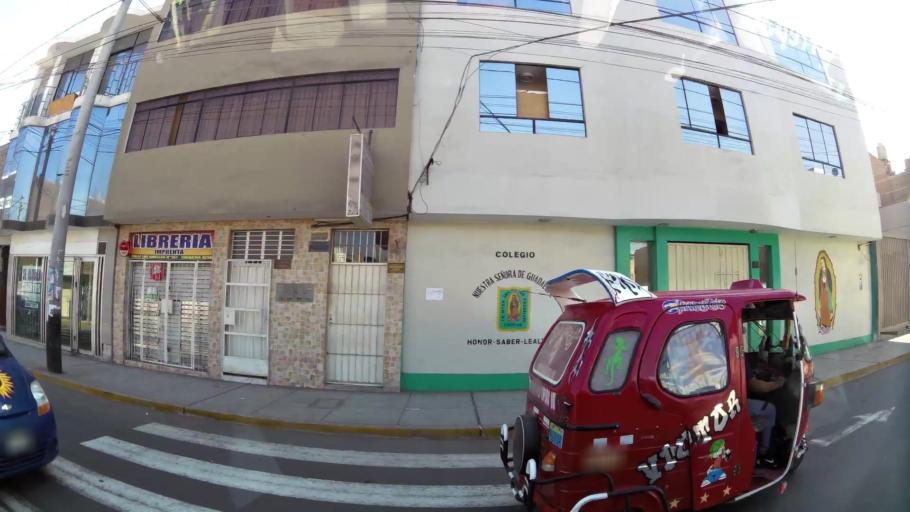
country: PE
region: Ica
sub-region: Provincia de Chincha
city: Chincha Alta
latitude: -13.4166
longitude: -76.1317
